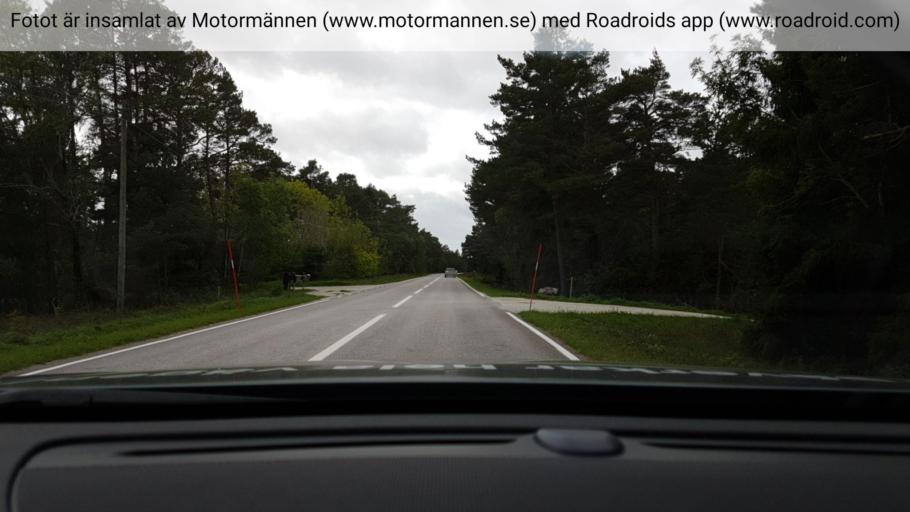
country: SE
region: Gotland
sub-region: Gotland
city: Klintehamn
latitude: 57.3215
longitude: 18.1860
